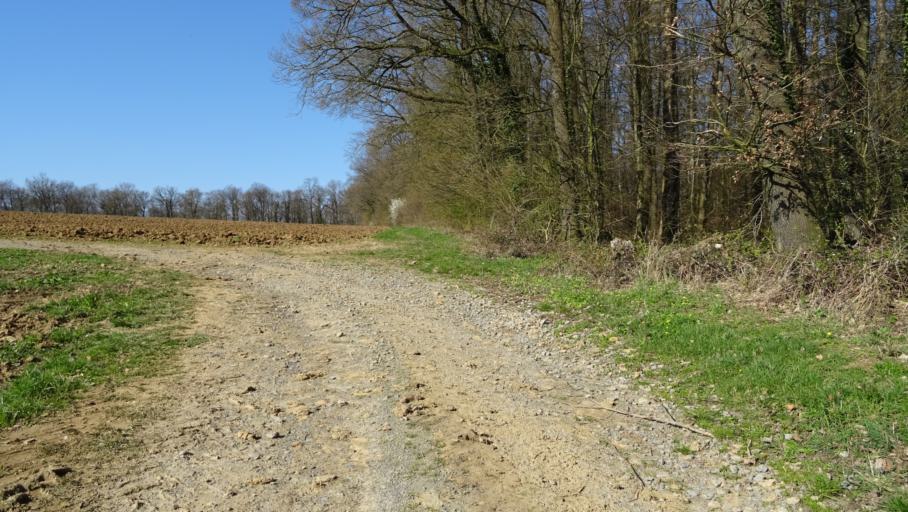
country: DE
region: Baden-Wuerttemberg
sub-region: Karlsruhe Region
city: Binau
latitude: 49.3624
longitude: 9.0413
